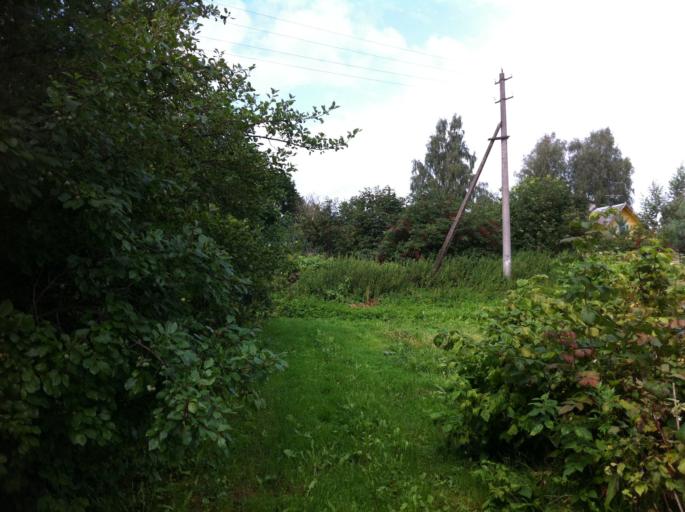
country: RU
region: Pskov
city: Izborsk
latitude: 57.8173
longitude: 27.9587
